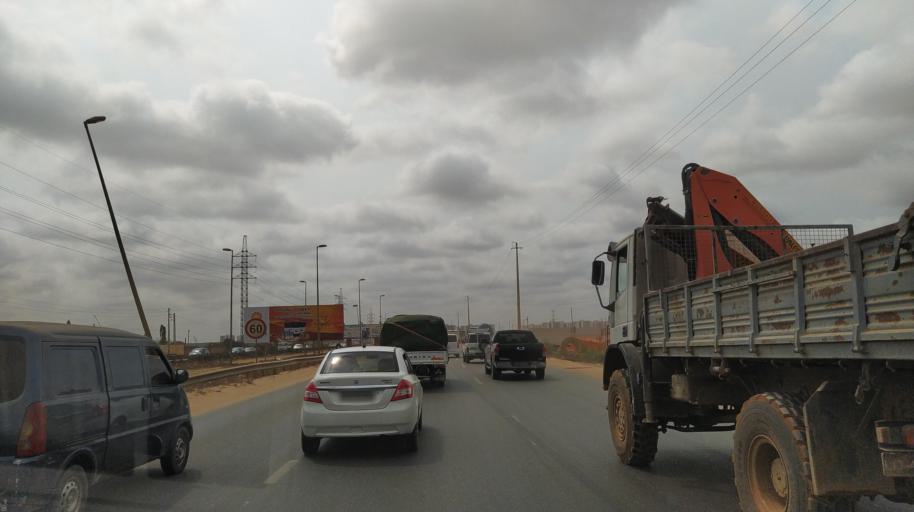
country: AO
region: Luanda
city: Luanda
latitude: -8.9771
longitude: 13.3820
